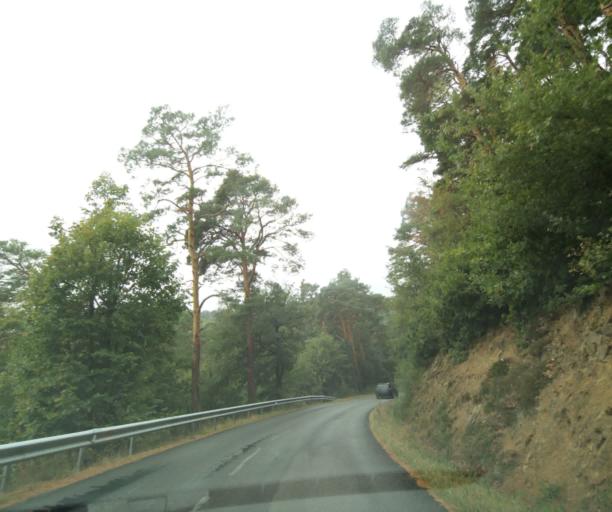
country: FR
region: Auvergne
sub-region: Departement du Puy-de-Dome
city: Durtol
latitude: 45.7931
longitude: 3.0411
